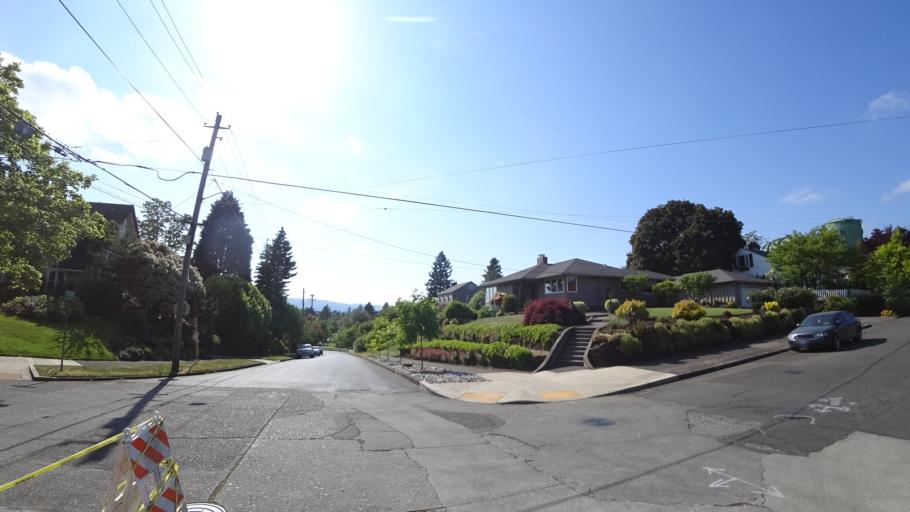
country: US
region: Oregon
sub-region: Multnomah County
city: Portland
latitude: 45.5531
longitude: -122.6448
